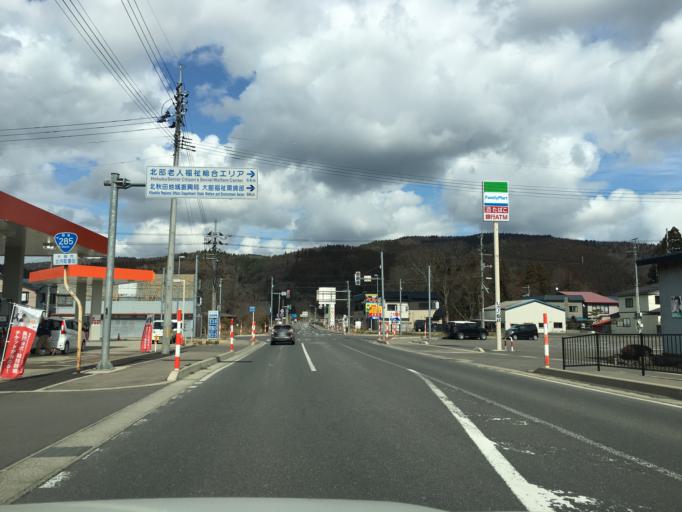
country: JP
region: Akita
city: Odate
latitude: 40.2252
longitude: 140.5895
